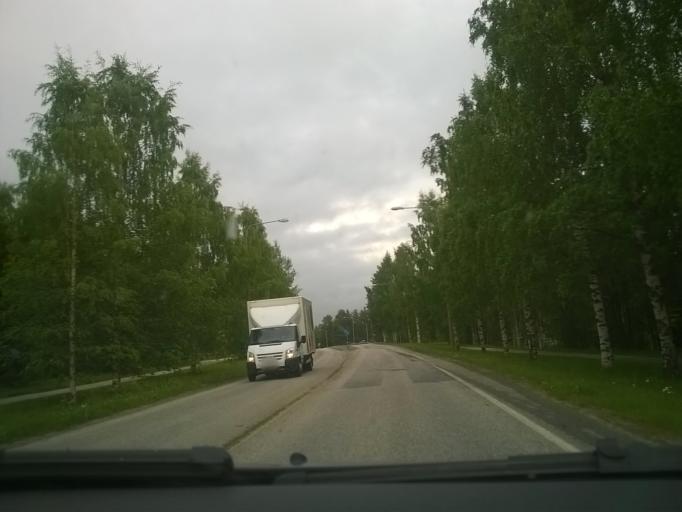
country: FI
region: Kainuu
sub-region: Kehys-Kainuu
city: Kuhmo
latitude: 64.1303
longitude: 29.4681
